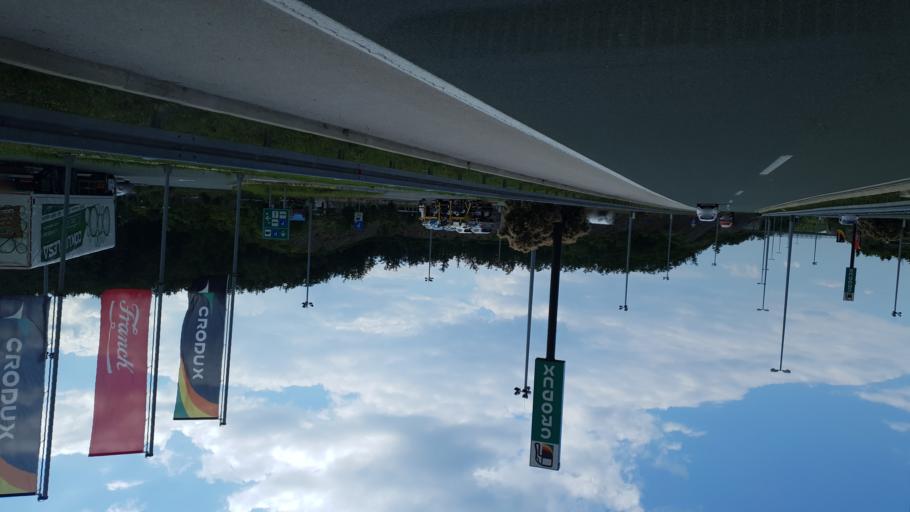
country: HR
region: Primorsko-Goranska
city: Matulji
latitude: 45.4439
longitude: 14.2737
